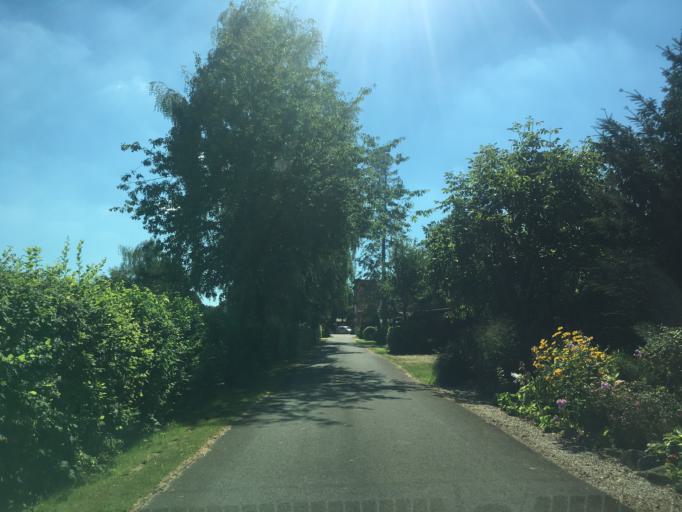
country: DE
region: North Rhine-Westphalia
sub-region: Regierungsbezirk Munster
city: Greven
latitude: 52.0228
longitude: 7.5799
